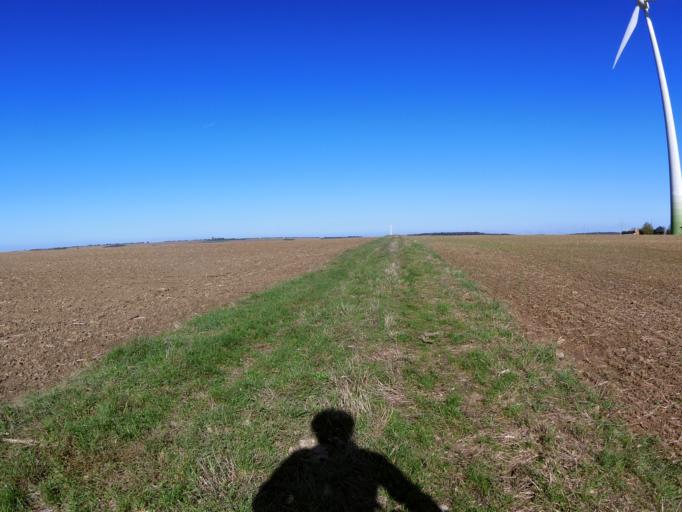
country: DE
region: Bavaria
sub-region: Regierungsbezirk Unterfranken
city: Theilheim
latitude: 49.7468
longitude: 10.0437
